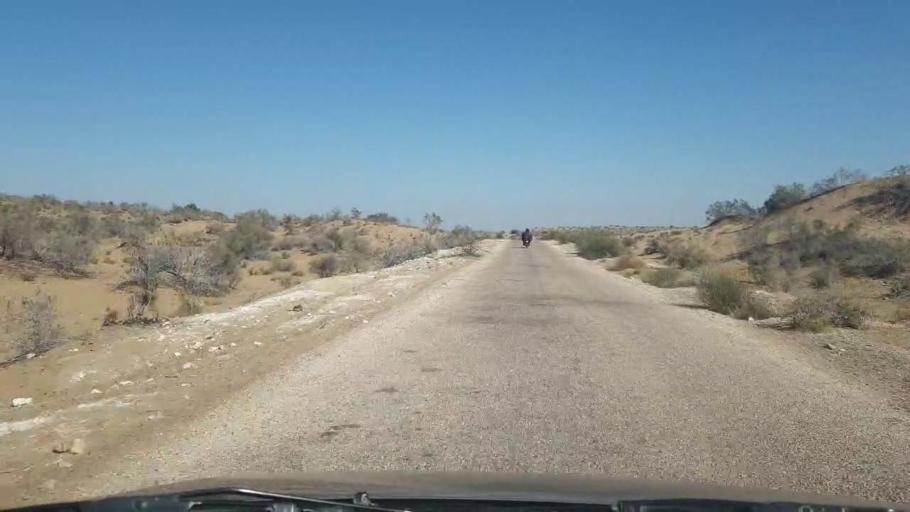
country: PK
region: Sindh
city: Bozdar
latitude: 27.0043
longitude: 68.8687
